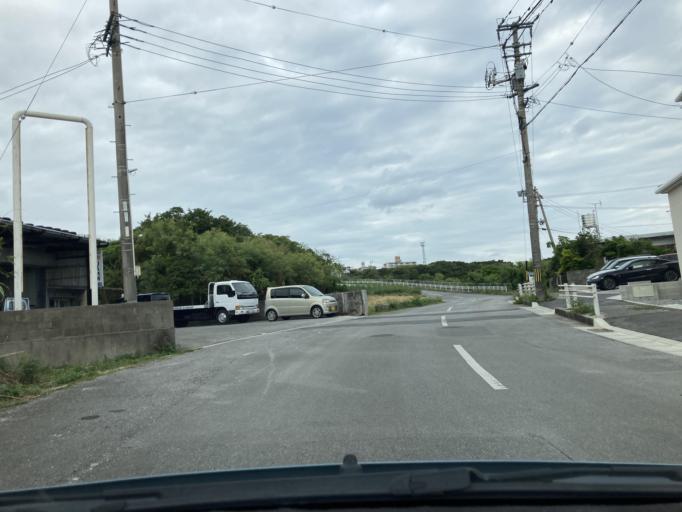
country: JP
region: Okinawa
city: Tomigusuku
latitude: 26.1382
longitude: 127.7912
